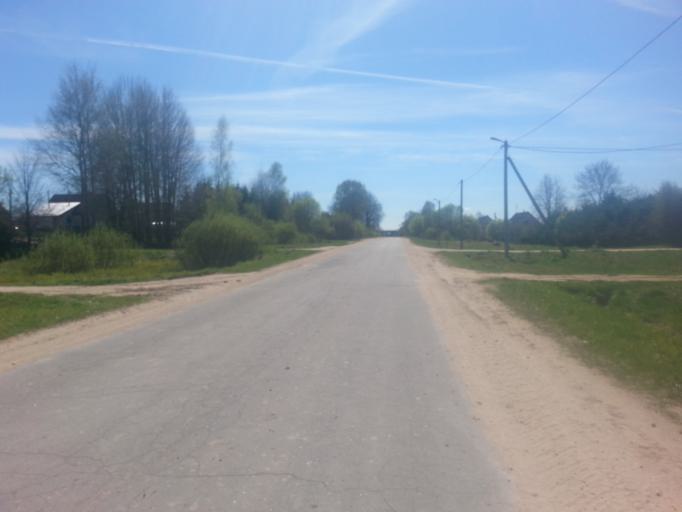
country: BY
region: Minsk
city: Narach
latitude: 54.9443
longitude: 26.6951
